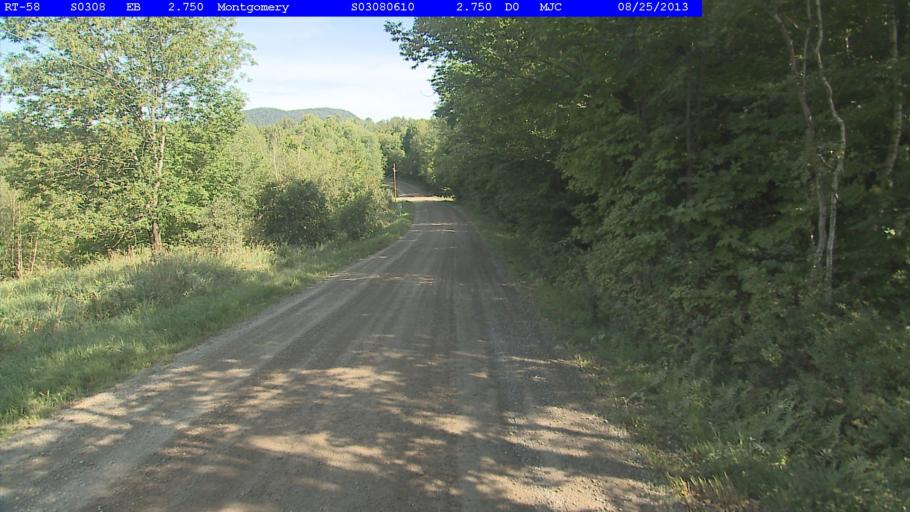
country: US
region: Vermont
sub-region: Franklin County
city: Richford
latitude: 44.8594
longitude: -72.5621
